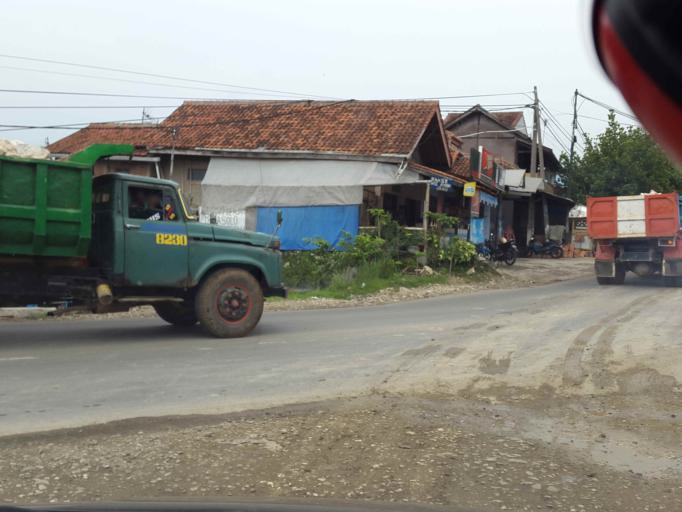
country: ID
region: West Java
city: Padalarang
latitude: -6.8348
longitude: 107.4251
